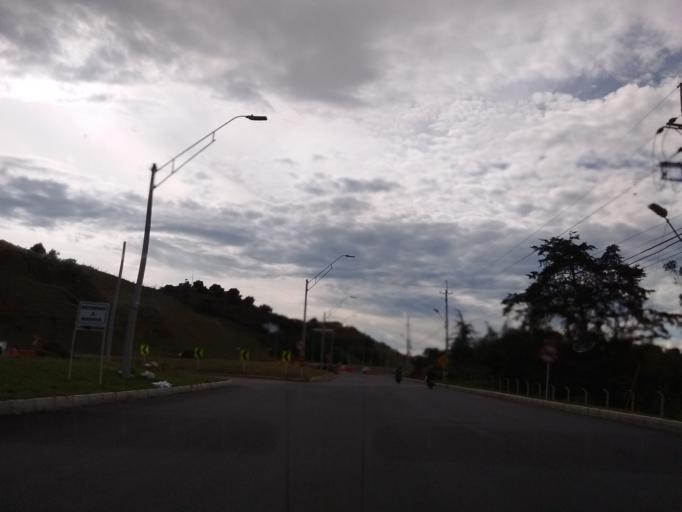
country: CO
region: Antioquia
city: Santuario
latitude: 6.1359
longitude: -75.2952
